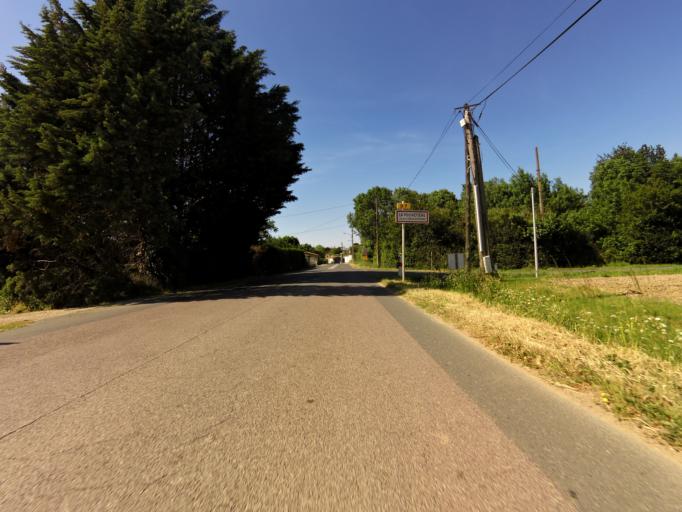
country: FR
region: Pays de la Loire
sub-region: Departement de la Loire-Atlantique
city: Le Loroux-Bottereau
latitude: 47.2107
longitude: -1.3536
